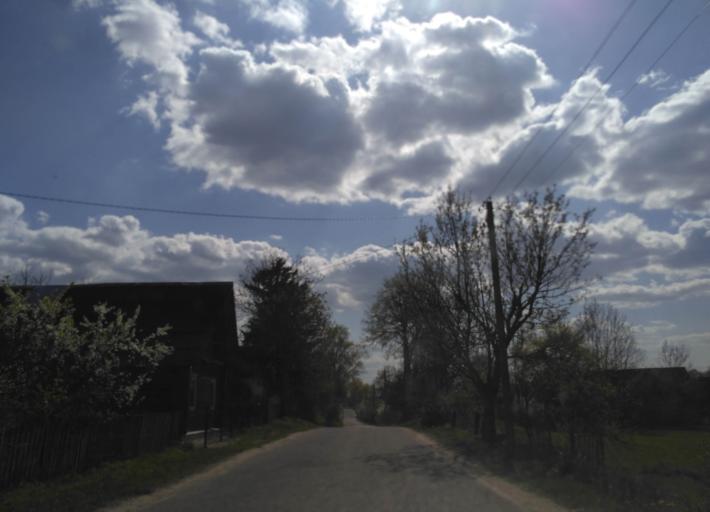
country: BY
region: Minsk
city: Narach
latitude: 54.9751
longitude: 26.6419
